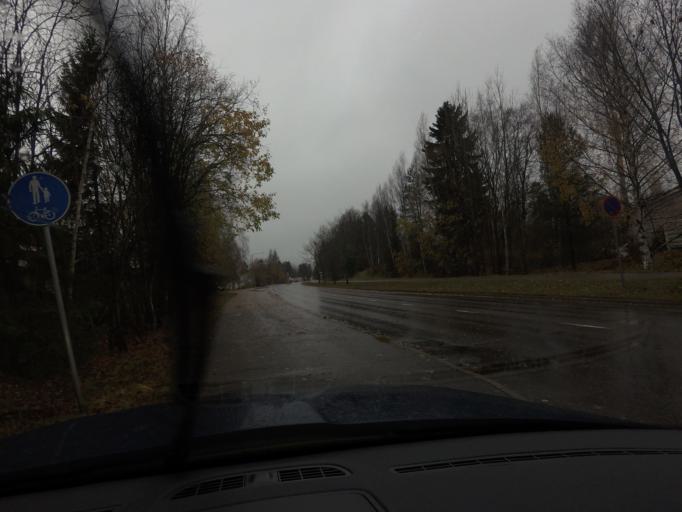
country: FI
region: Uusimaa
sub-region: Helsinki
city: Espoo
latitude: 60.1954
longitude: 24.6737
